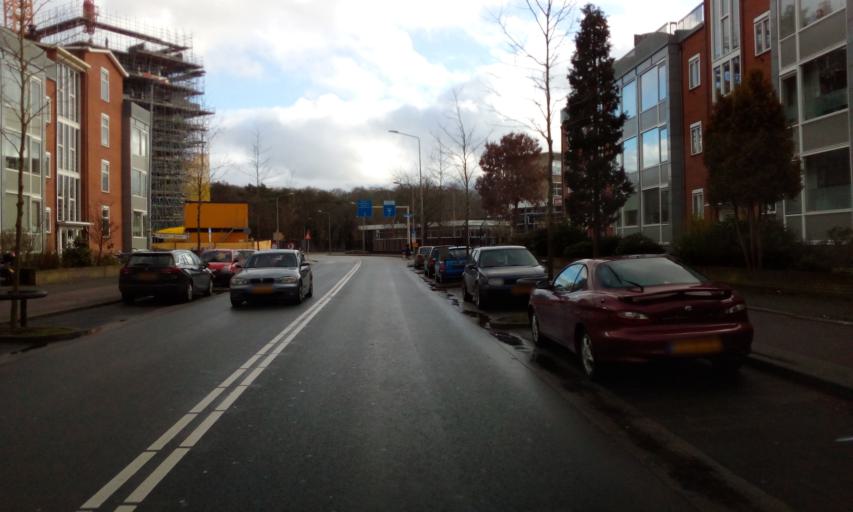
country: NL
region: North Holland
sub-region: Gemeente Hilversum
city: Hilversum
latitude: 52.2158
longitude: 5.1974
